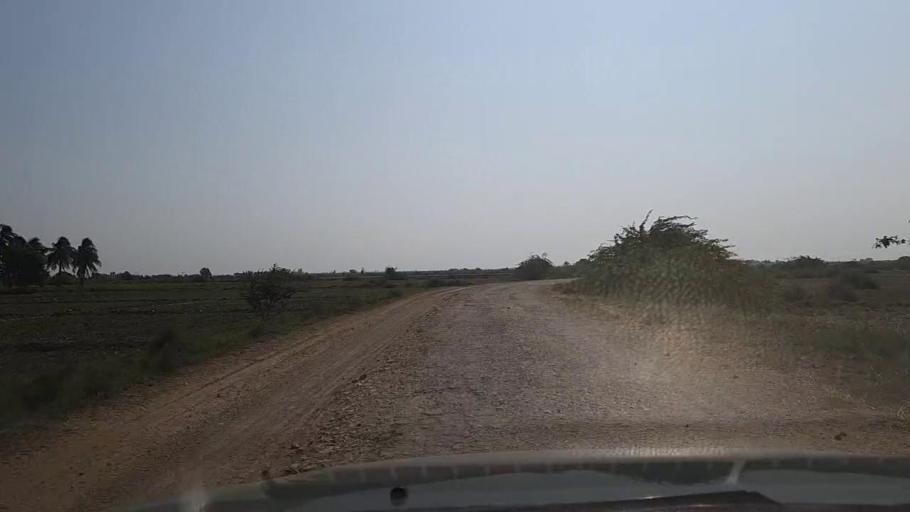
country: PK
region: Sindh
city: Mirpur Sakro
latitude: 24.3901
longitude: 67.6652
